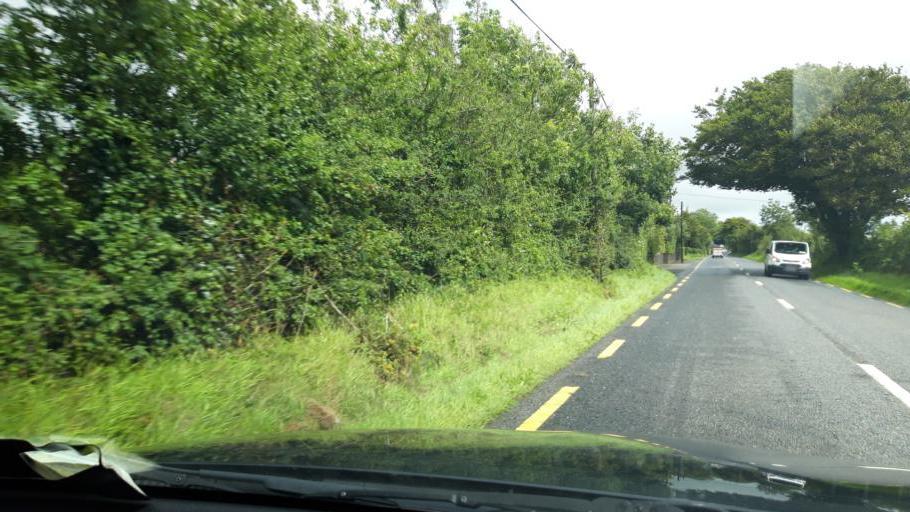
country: IE
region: Leinster
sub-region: Loch Garman
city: New Ross
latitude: 52.4334
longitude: -6.7672
